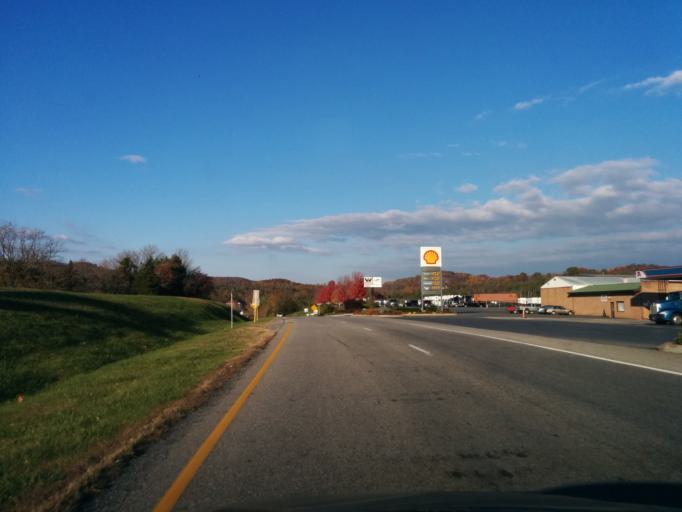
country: US
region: Virginia
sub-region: Rockbridge County
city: East Lexington
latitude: 37.8320
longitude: -79.3784
